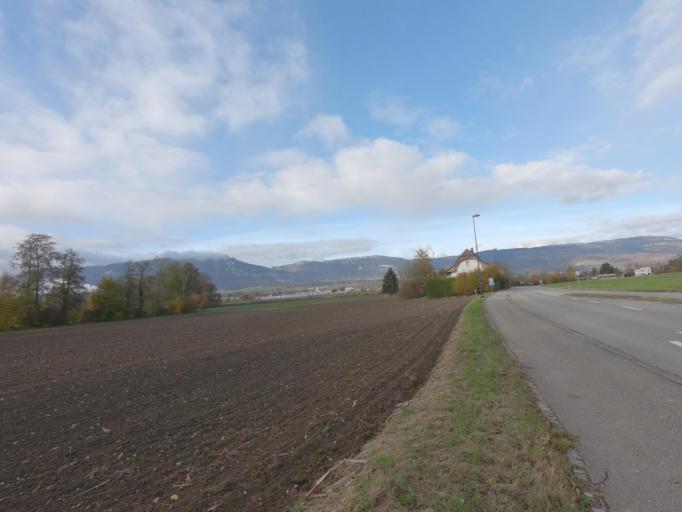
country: CH
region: Solothurn
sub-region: Bezirk Wasseramt
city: Luterbach
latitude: 47.2061
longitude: 7.5841
